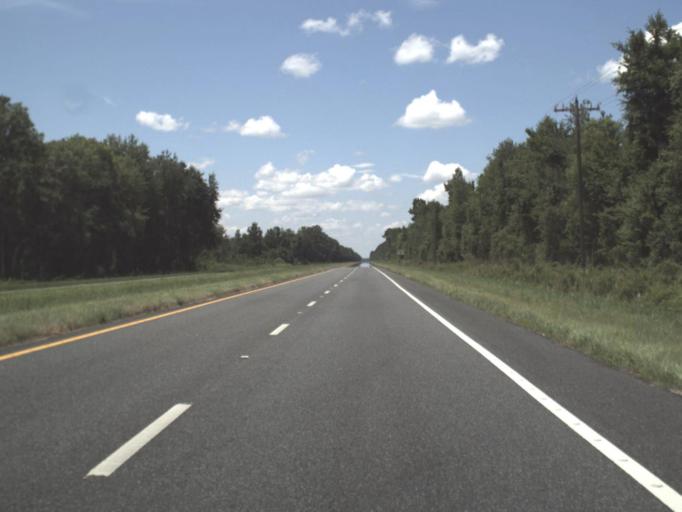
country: US
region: Florida
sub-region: Taylor County
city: Perry
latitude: 30.2629
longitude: -83.7114
